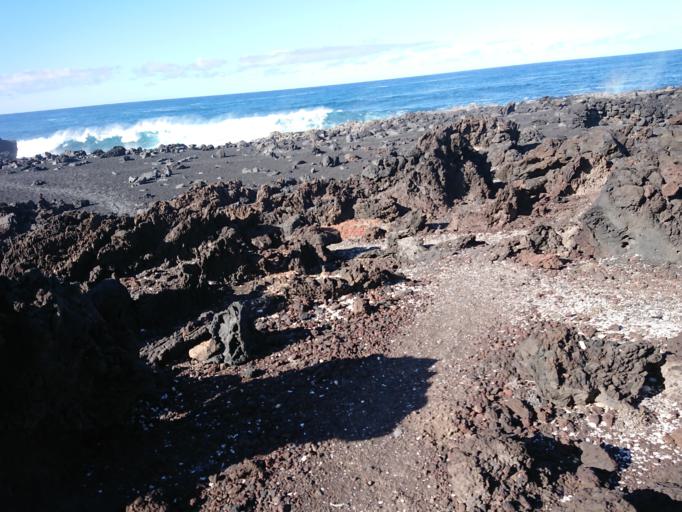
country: ES
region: Canary Islands
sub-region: Provincia de Las Palmas
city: Tinajo
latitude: 29.0812
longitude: -13.7308
